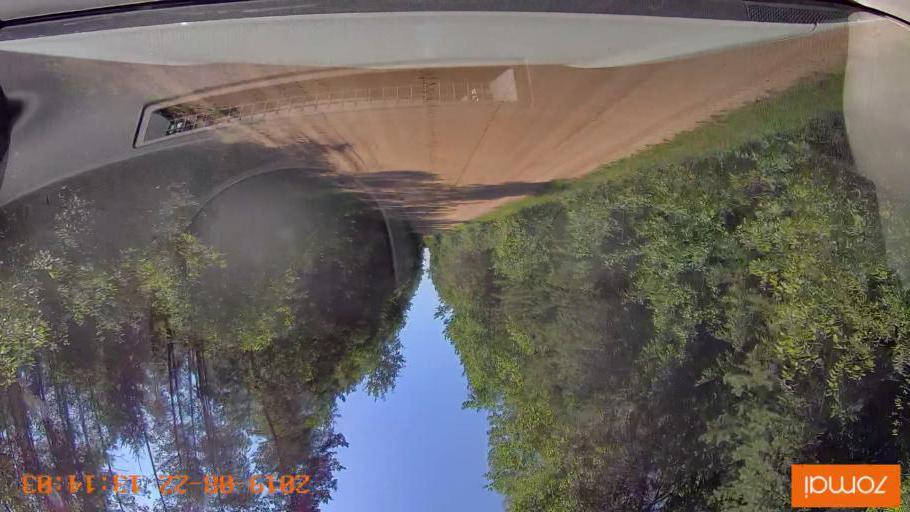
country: BY
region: Minsk
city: Prawdzinski
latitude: 53.2713
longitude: 27.8828
